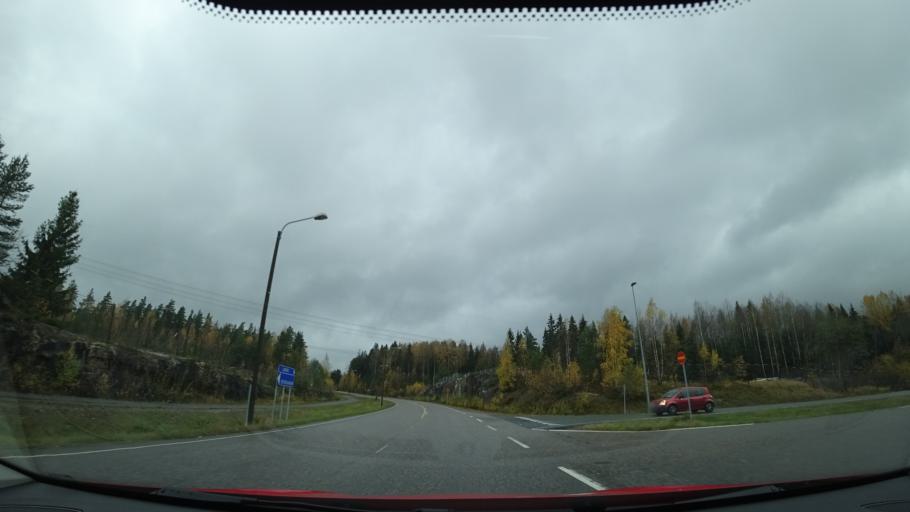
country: FI
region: Uusimaa
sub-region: Helsinki
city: Sibbo
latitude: 60.2675
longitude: 25.2089
